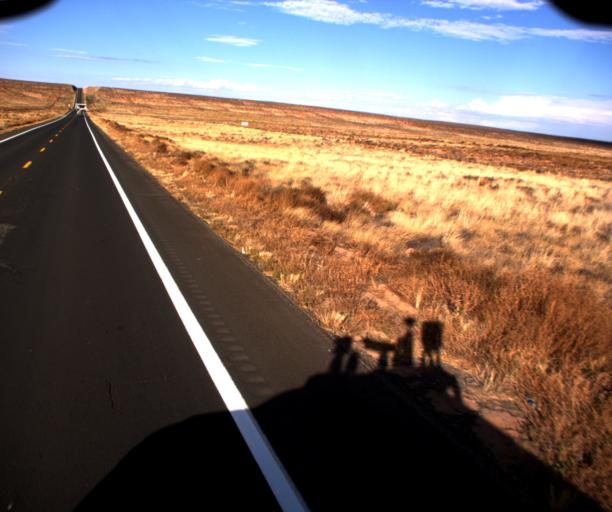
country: US
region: Arizona
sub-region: Apache County
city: Lukachukai
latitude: 36.9625
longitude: -109.4321
